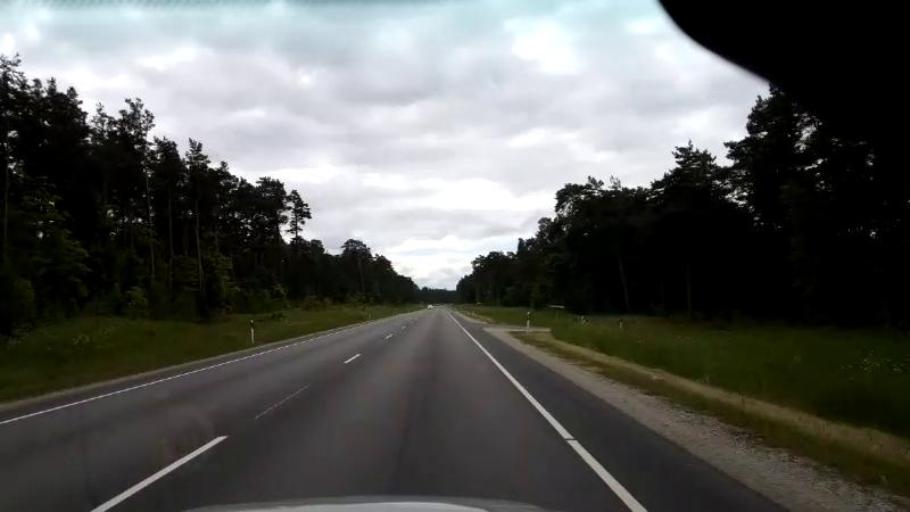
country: EE
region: Paernumaa
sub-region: Paernu linn
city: Parnu
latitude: 58.1942
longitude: 24.4889
